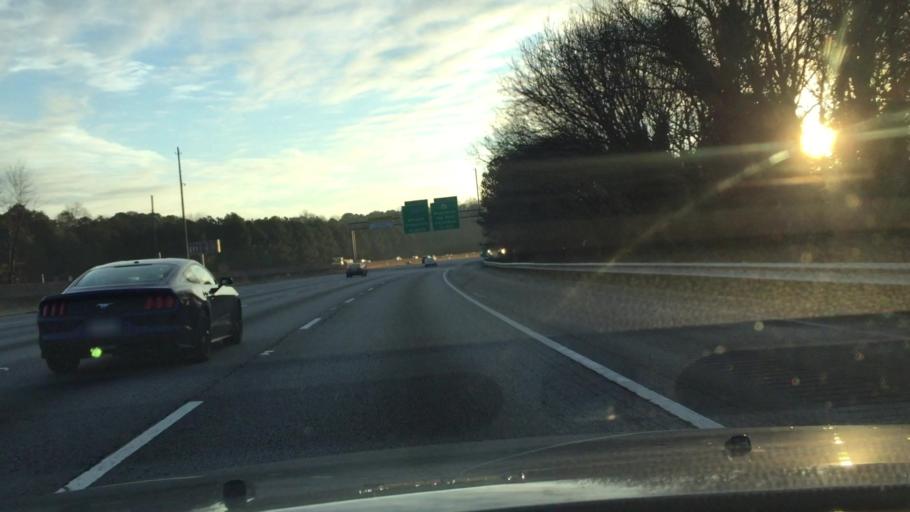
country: US
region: Georgia
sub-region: DeKalb County
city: Doraville
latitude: 33.9201
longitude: -84.2981
